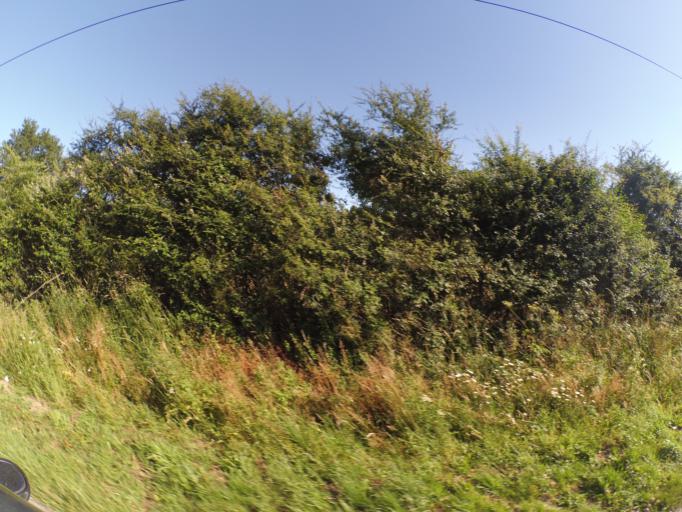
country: FR
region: Pays de la Loire
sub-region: Departement de la Vendee
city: Beaurepaire
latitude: 46.9066
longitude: -1.1240
